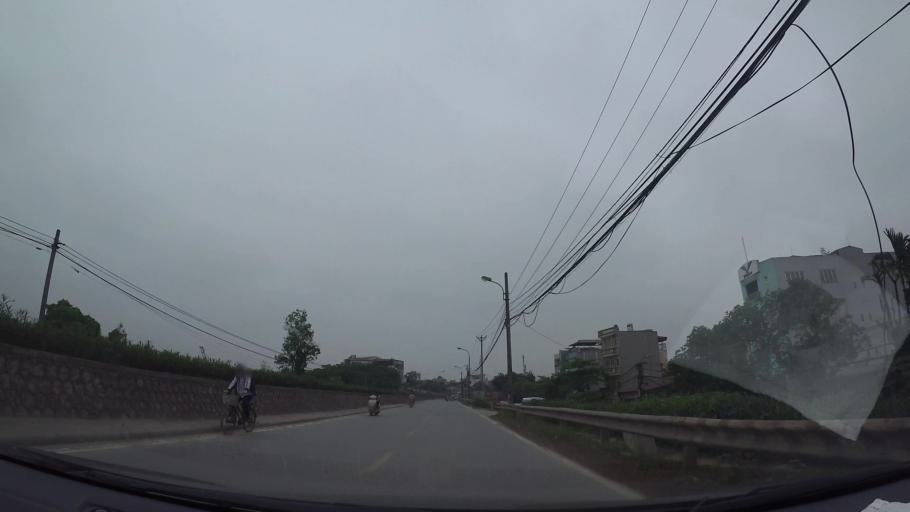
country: VN
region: Ha Noi
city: Hai BaTrung
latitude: 20.9972
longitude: 105.8906
